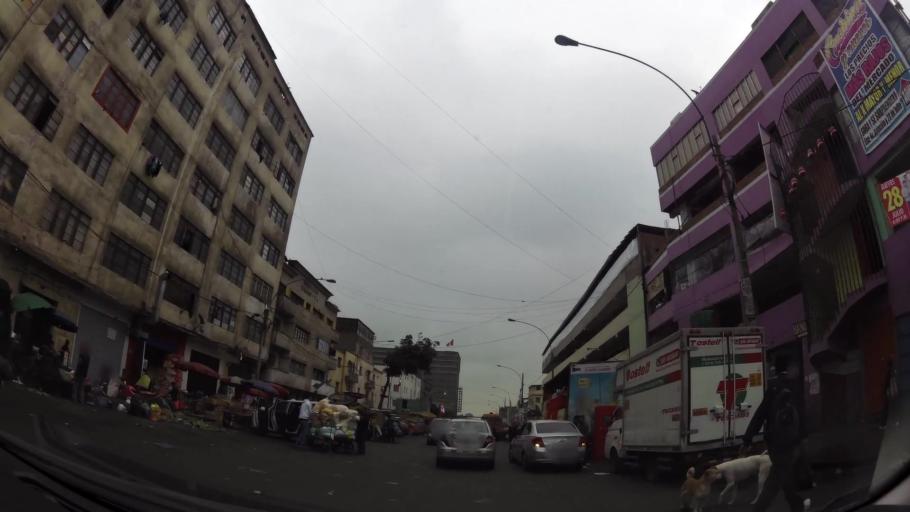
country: PE
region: Lima
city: Lima
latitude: -12.0610
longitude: -77.0132
